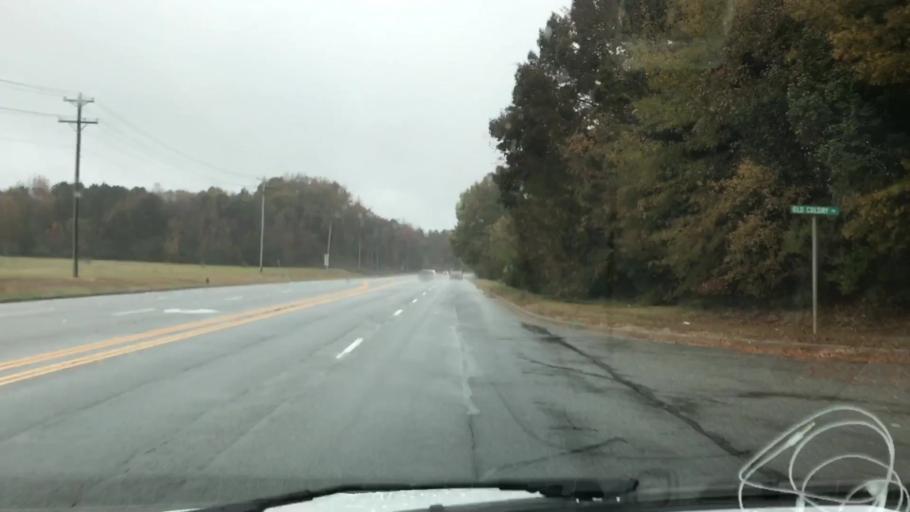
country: US
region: South Carolina
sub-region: Laurens County
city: Clinton
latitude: 34.4671
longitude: -81.8524
